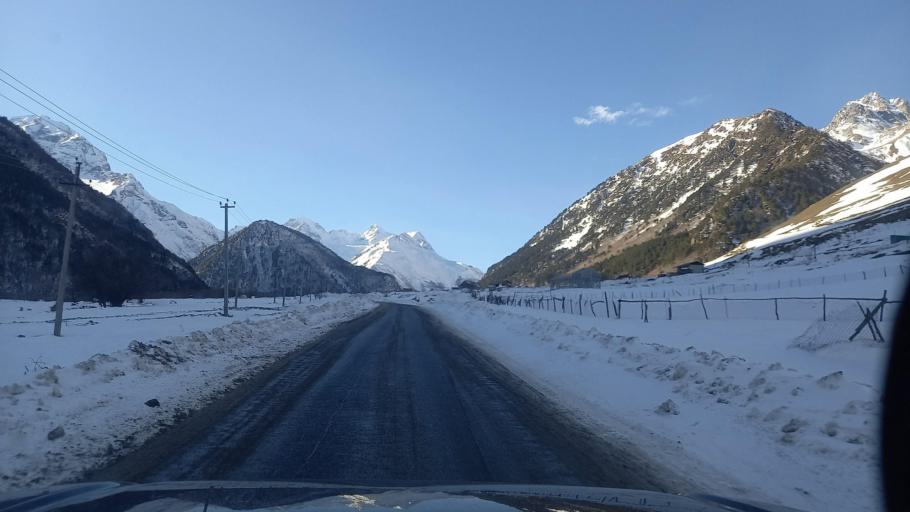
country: RU
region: Kabardino-Balkariya
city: Verkhnyaya Balkariya
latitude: 42.9015
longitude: 43.6335
